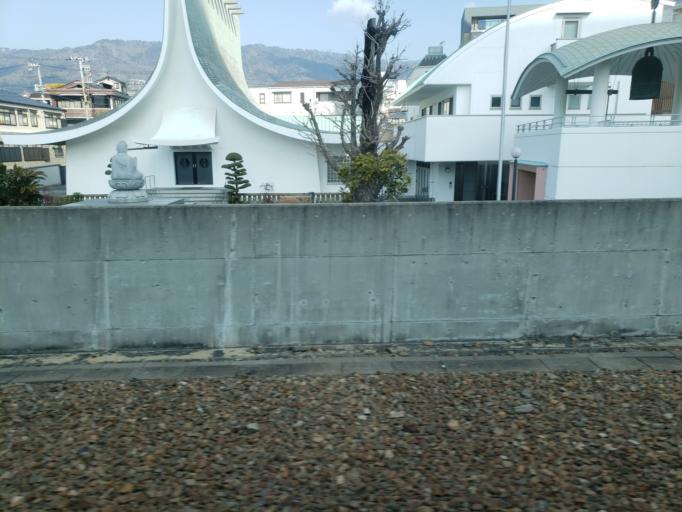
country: JP
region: Hyogo
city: Ashiya
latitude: 34.7193
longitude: 135.2603
